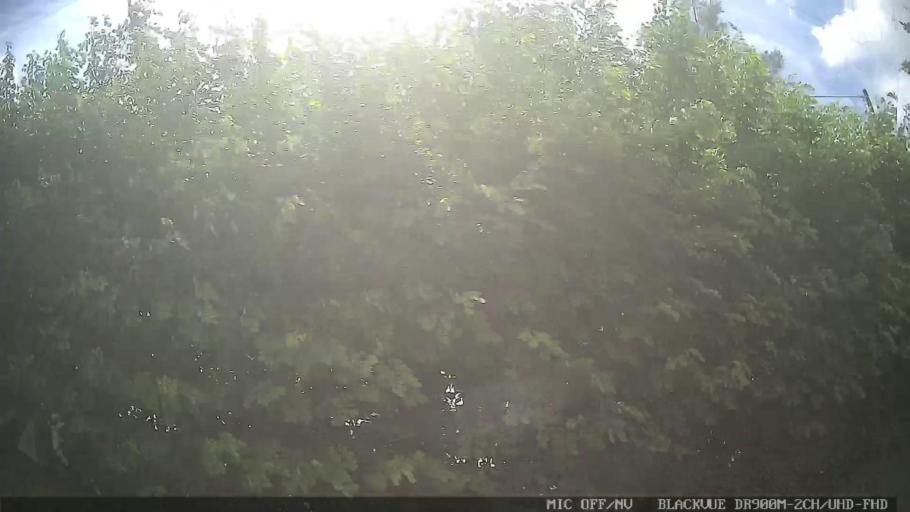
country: BR
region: Sao Paulo
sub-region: Braganca Paulista
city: Braganca Paulista
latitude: -22.9549
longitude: -46.6156
